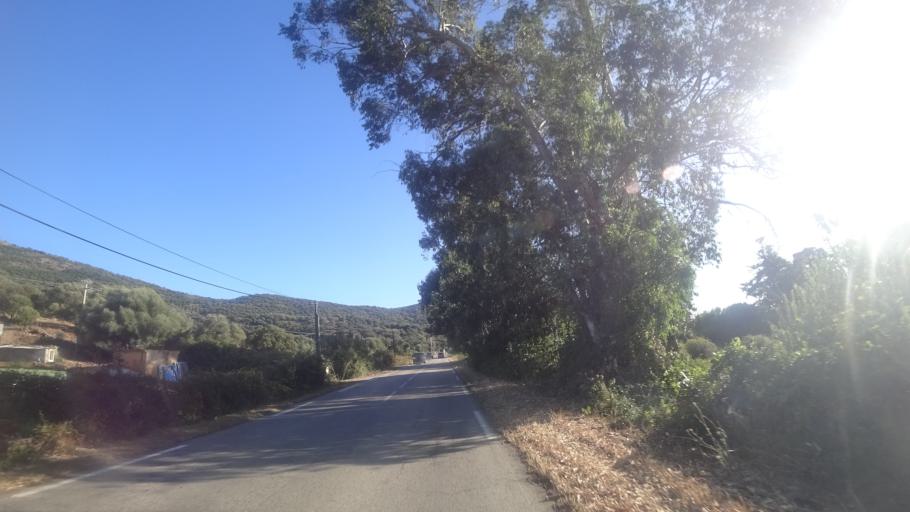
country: FR
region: Corsica
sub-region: Departement de la Corse-du-Sud
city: Cargese
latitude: 42.1752
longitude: 8.6119
